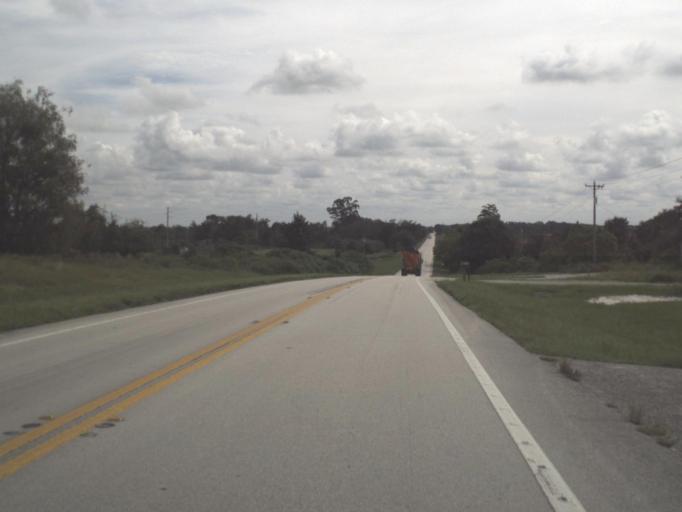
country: US
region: Florida
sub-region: Highlands County
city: Lake Placid
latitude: 27.2083
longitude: -81.2944
